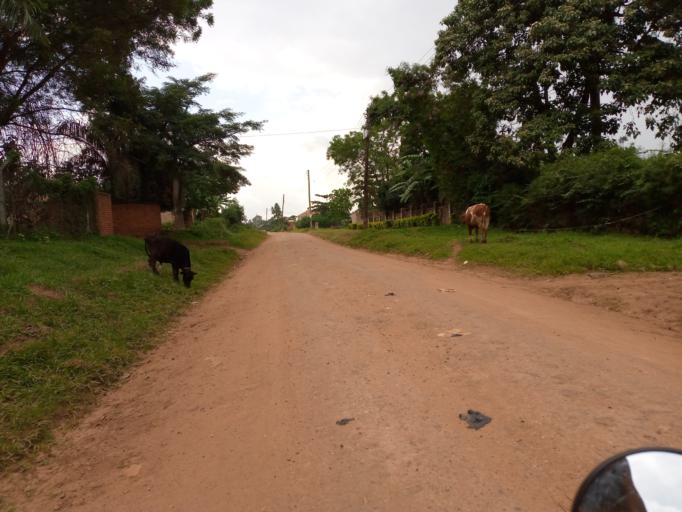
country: UG
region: Eastern Region
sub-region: Mbale District
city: Mbale
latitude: 1.0818
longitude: 34.1737
